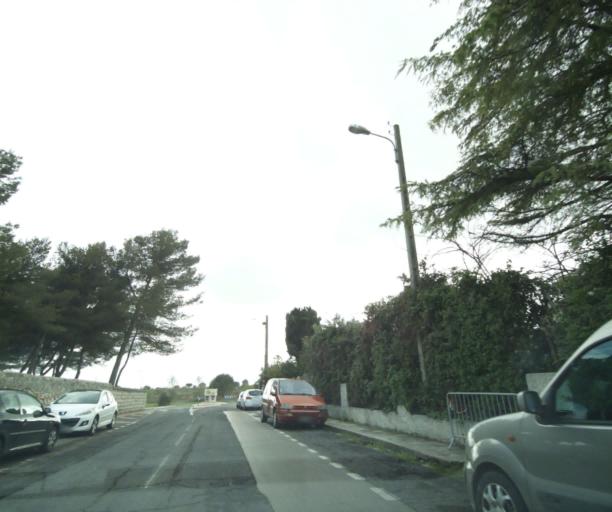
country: FR
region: Languedoc-Roussillon
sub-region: Departement de l'Herault
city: Pignan
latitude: 43.5810
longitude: 3.7594
